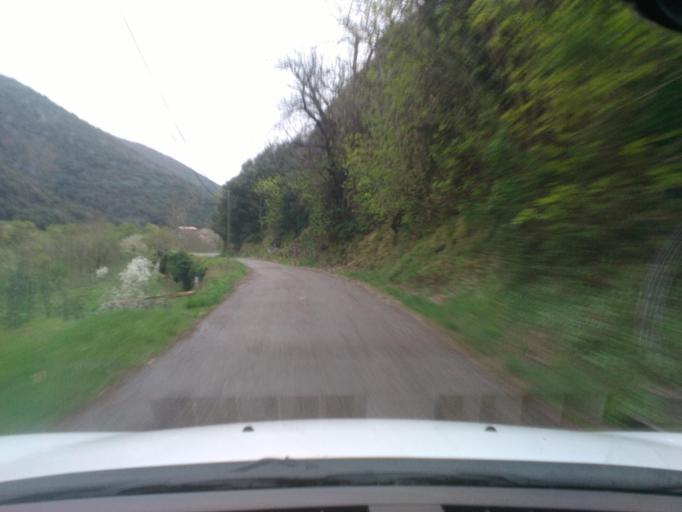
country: FR
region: Languedoc-Roussillon
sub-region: Departement du Gard
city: Valleraugue
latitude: 44.0978
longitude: 3.6318
